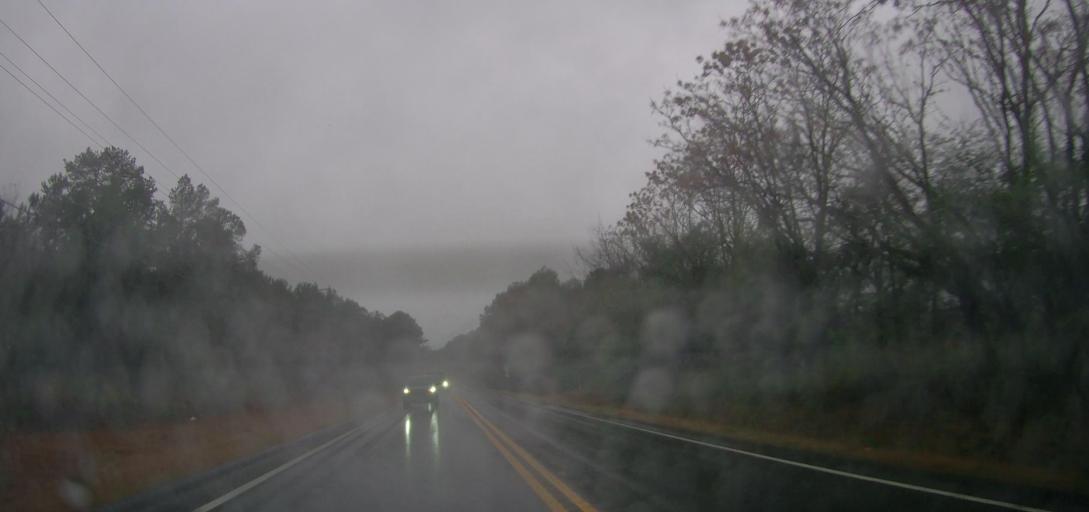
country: US
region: Georgia
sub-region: Putnam County
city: Eatonton
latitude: 33.2875
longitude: -83.3924
